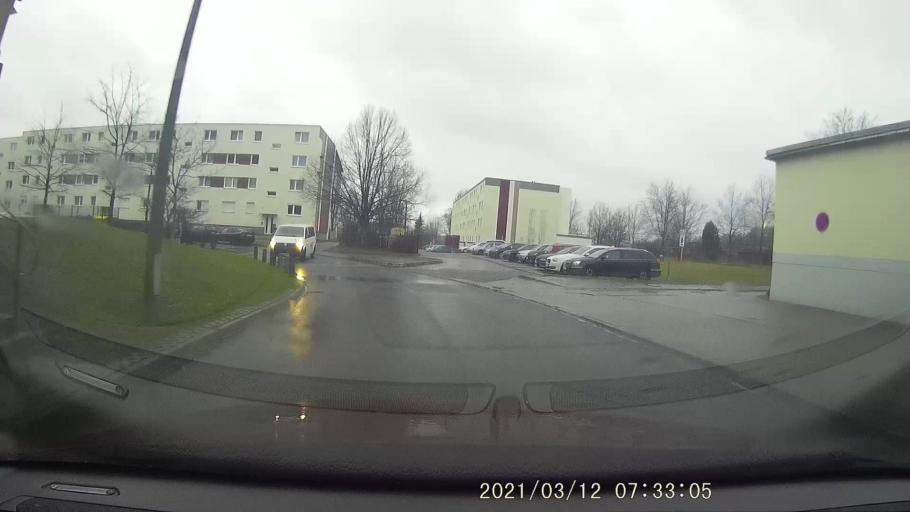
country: DE
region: Saxony
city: Goerlitz
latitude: 51.1644
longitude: 14.9781
